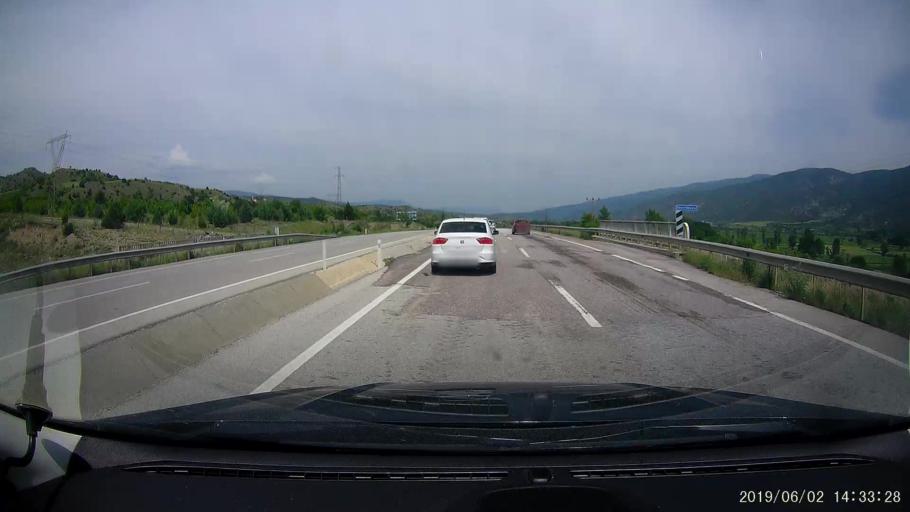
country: TR
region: Kastamonu
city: Tosya
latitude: 41.0317
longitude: 34.1715
